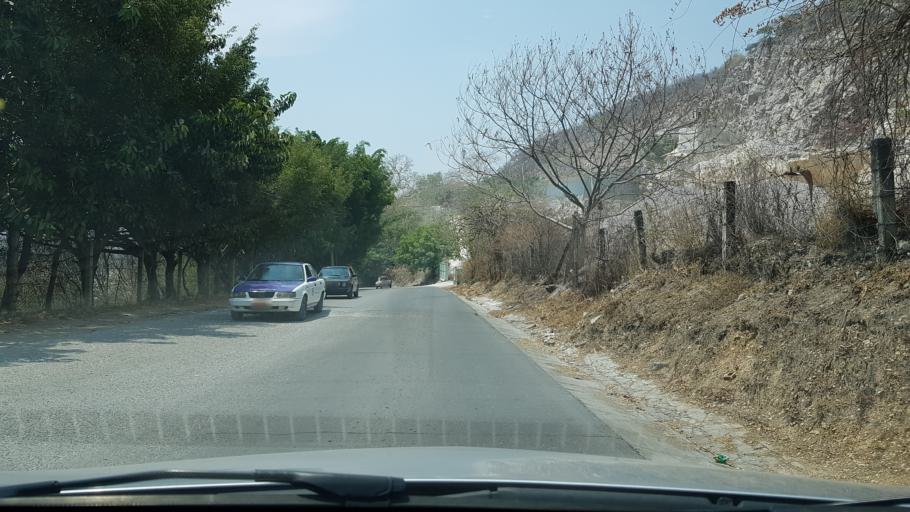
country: MX
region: Morelos
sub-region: Jiutepec
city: Jiutepec
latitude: 18.8710
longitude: -99.1733
